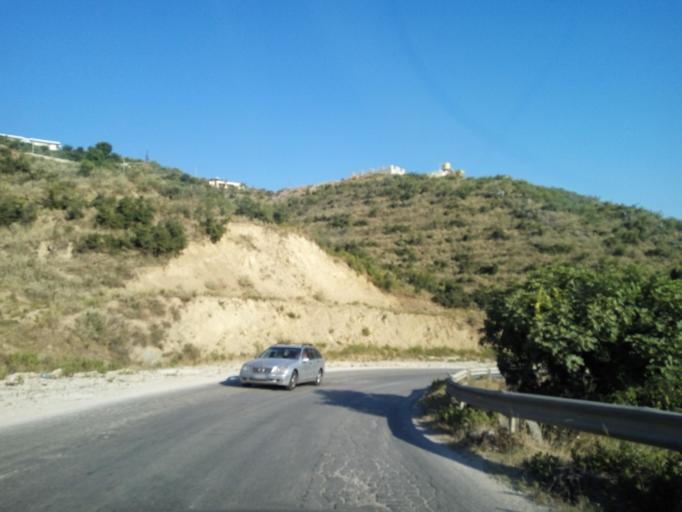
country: AL
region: Vlore
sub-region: Rrethi i Sarandes
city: Sarande
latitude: 39.8783
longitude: 20.0322
